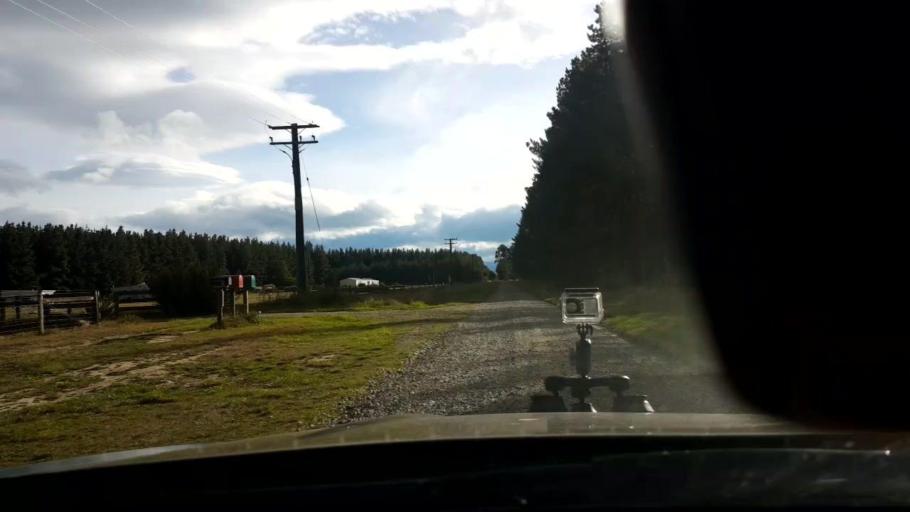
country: NZ
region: Canterbury
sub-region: Waimakariri District
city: Oxford
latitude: -43.3934
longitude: 172.2947
